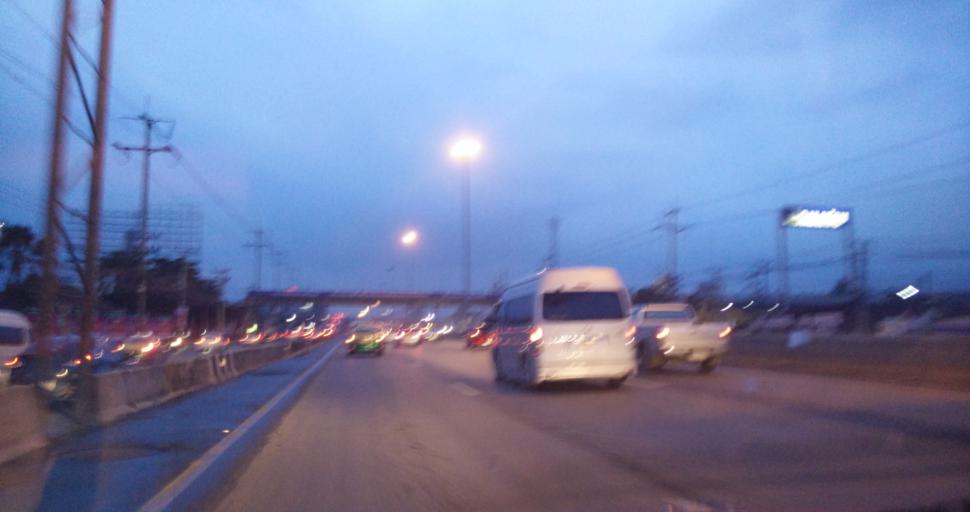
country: TH
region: Pathum Thani
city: Khlong Luang
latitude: 14.0292
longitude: 100.6158
